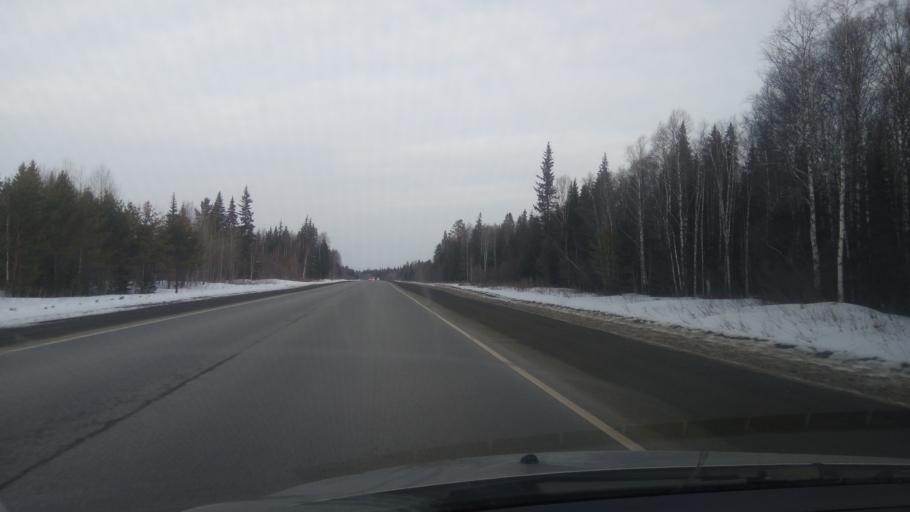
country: RU
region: Sverdlovsk
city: Atig
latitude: 56.8066
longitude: 59.3709
